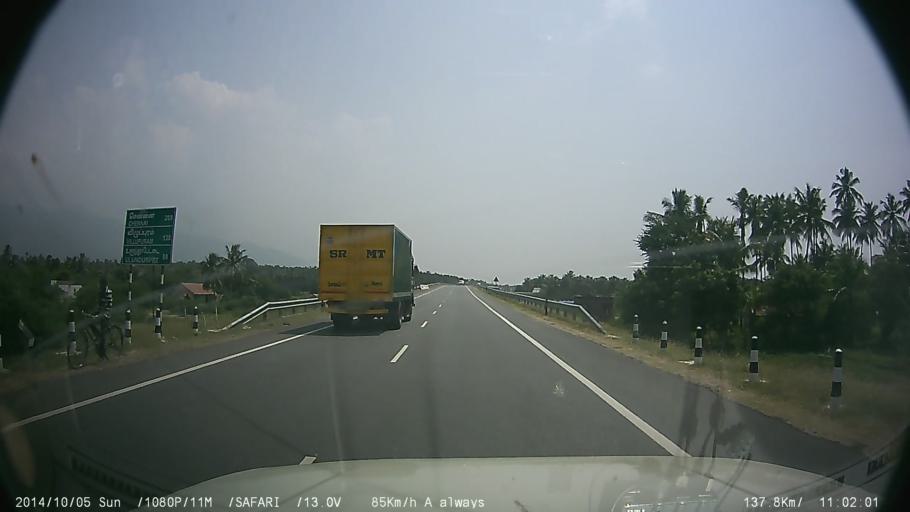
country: IN
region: Tamil Nadu
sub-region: Salem
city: Attur
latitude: 11.6139
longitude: 78.5668
